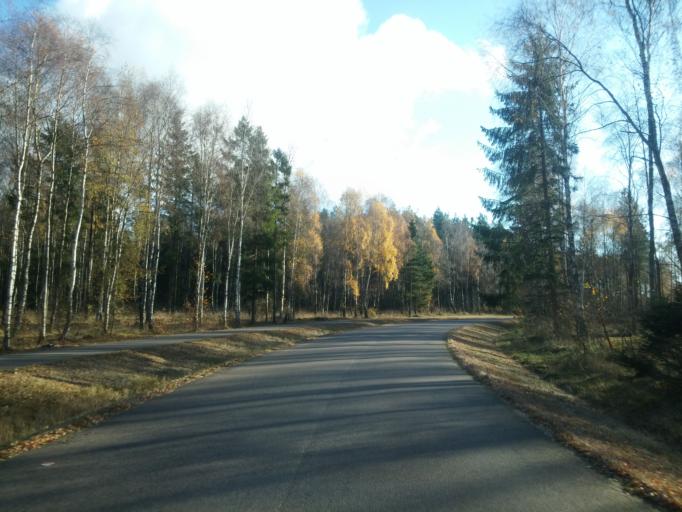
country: SE
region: Skane
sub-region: Angelholms Kommun
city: AEngelholm
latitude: 56.2338
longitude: 12.8300
